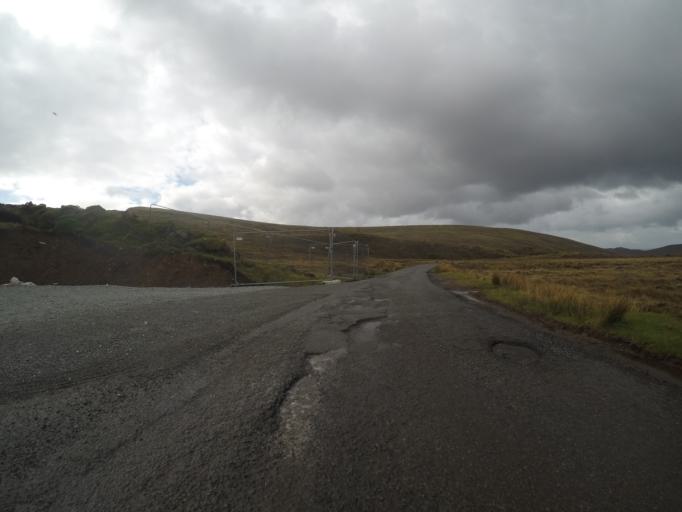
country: GB
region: Scotland
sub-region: Highland
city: Portree
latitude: 57.6265
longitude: -6.2940
